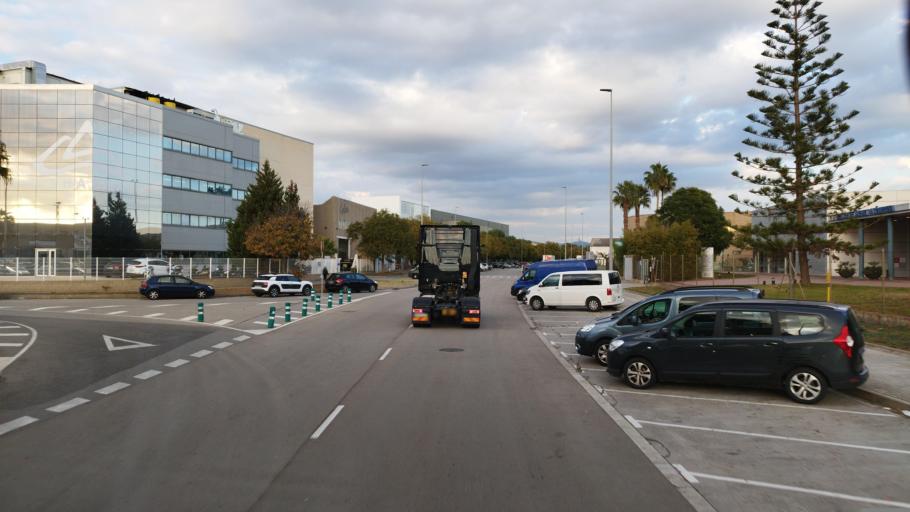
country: ES
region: Catalonia
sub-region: Provincia de Barcelona
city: Gava
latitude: 41.3003
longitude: 2.0129
